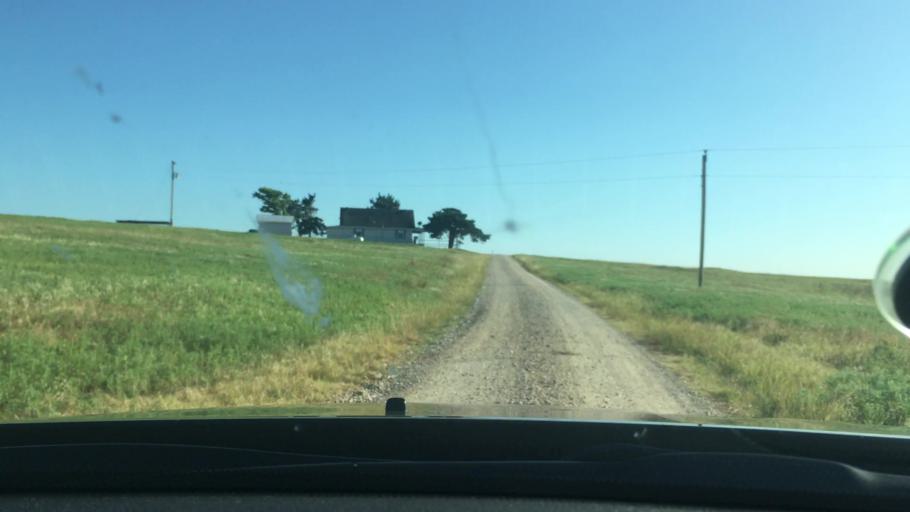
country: US
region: Oklahoma
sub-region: Johnston County
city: Tishomingo
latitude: 34.4134
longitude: -96.7633
